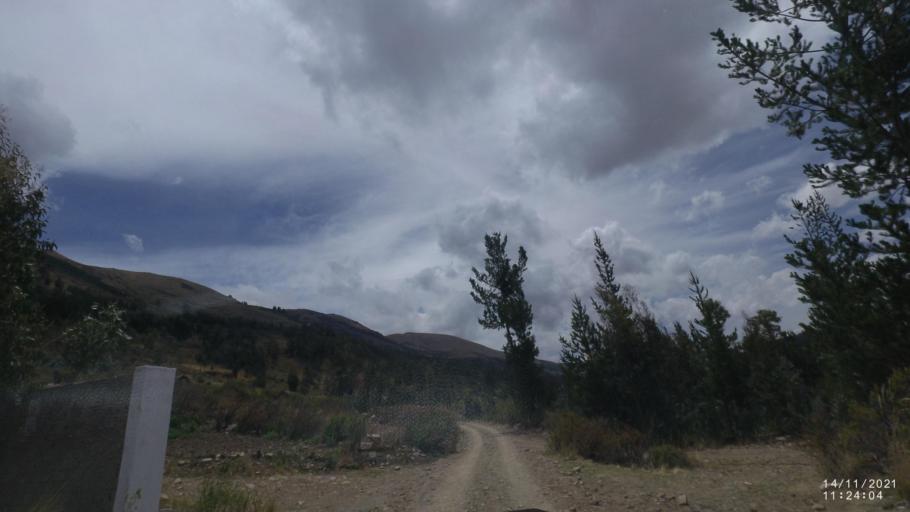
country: BO
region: Cochabamba
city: Cochabamba
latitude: -17.3344
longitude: -66.0278
